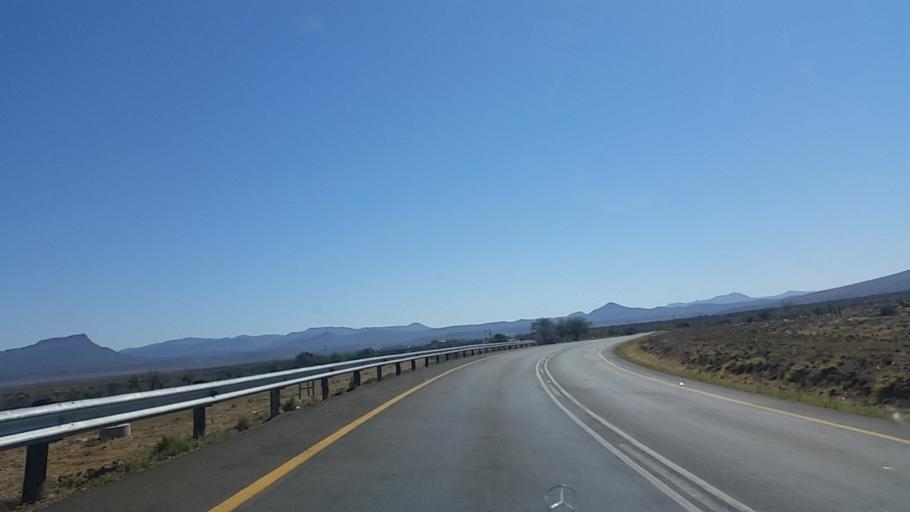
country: ZA
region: Eastern Cape
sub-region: Cacadu District Municipality
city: Graaff-Reinet
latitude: -32.2331
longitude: 24.5350
